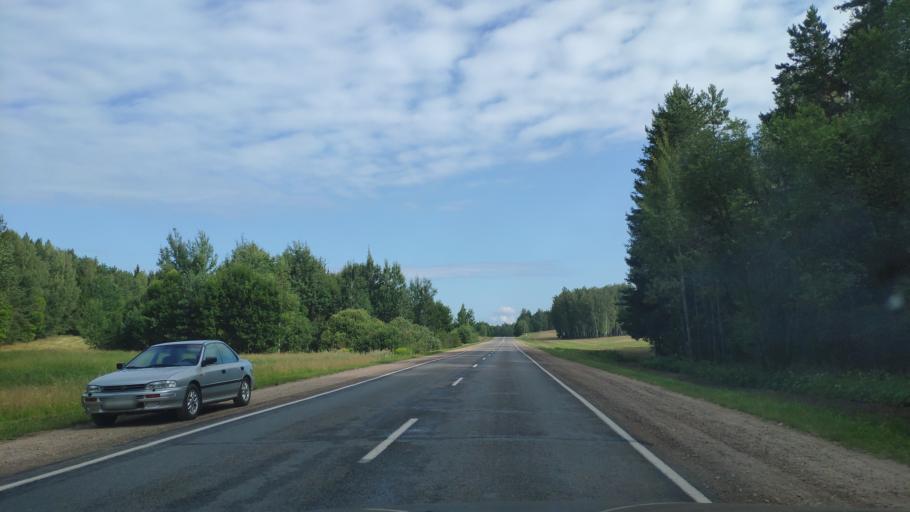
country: BY
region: Minsk
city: Zaslawye
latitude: 53.9588
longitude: 27.2452
